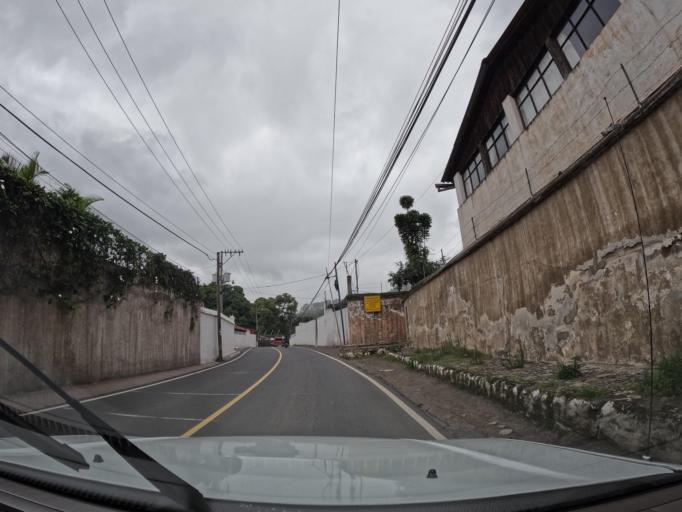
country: GT
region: Sacatepequez
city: Pastores
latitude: 14.5960
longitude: -90.7546
